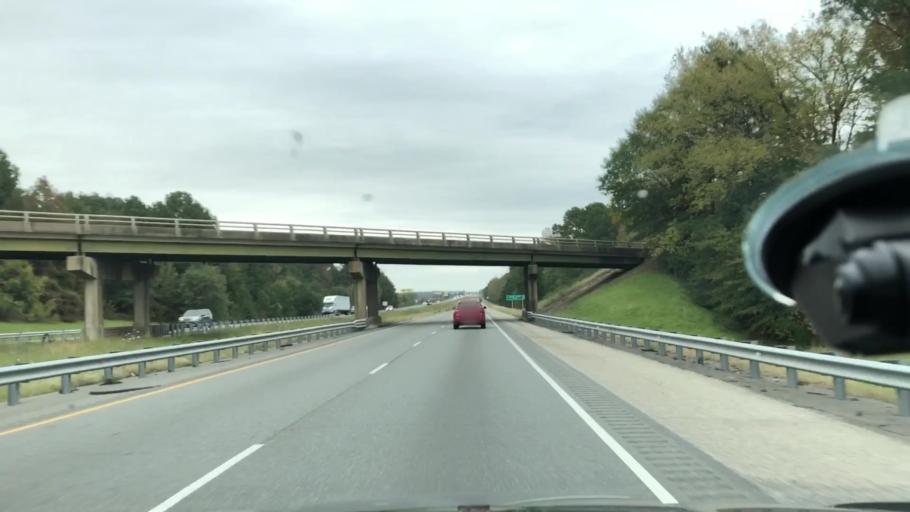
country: US
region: Arkansas
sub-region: Miller County
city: Texarkana
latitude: 33.4878
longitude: -93.9733
